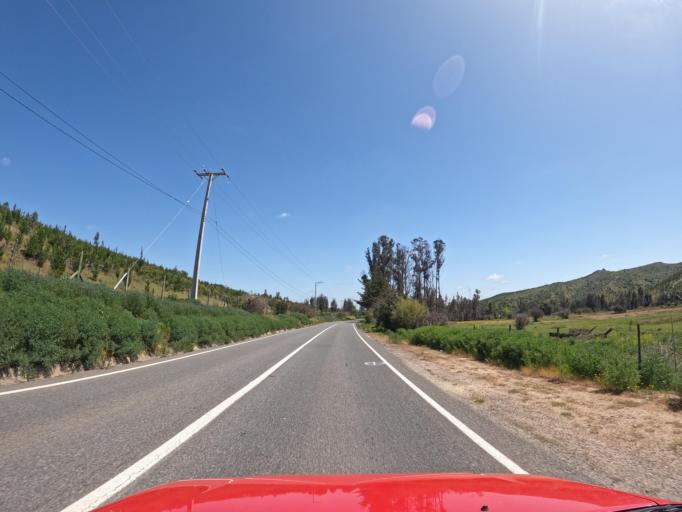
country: CL
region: O'Higgins
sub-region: Provincia de Colchagua
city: Santa Cruz
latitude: -34.6647
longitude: -71.8332
